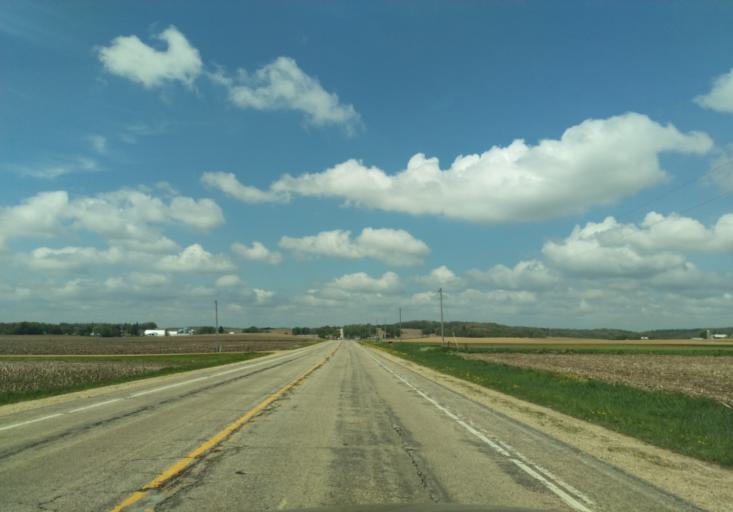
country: US
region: Wisconsin
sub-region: Dane County
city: Cross Plains
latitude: 43.0606
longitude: -89.6396
